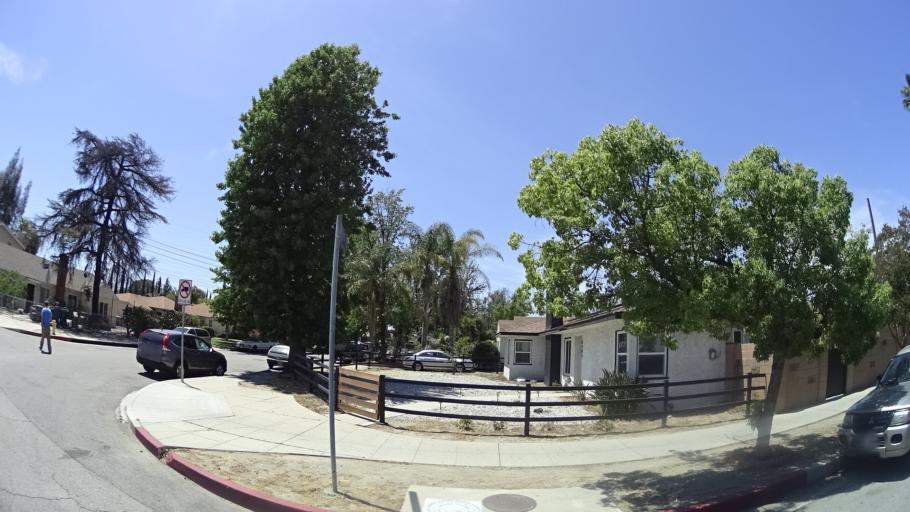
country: US
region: California
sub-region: Los Angeles County
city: North Hollywood
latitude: 34.1856
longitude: -118.3704
